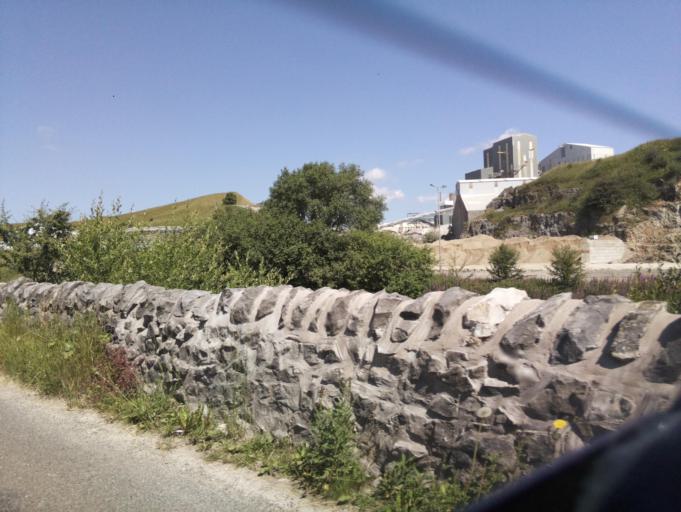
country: GB
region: England
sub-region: Derbyshire
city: Buxton
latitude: 53.2910
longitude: -1.8668
